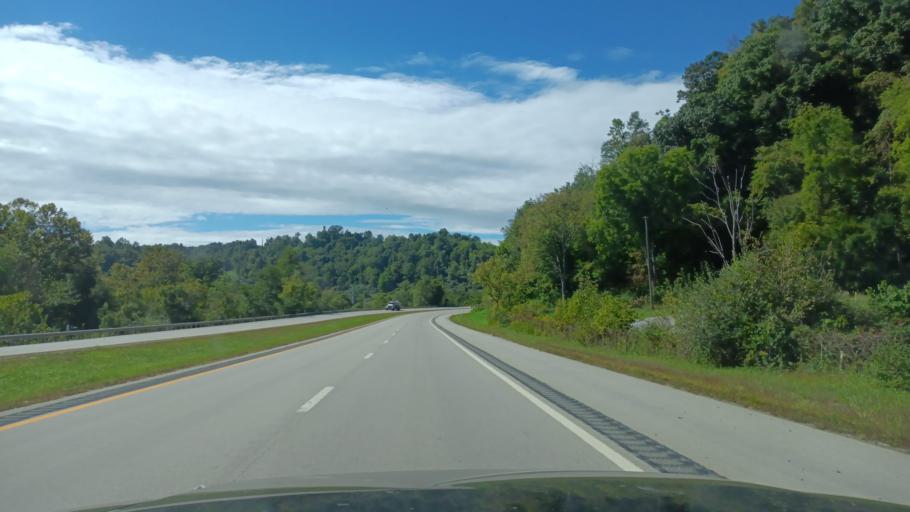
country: US
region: West Virginia
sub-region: Doddridge County
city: West Union
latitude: 39.2792
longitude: -80.6840
